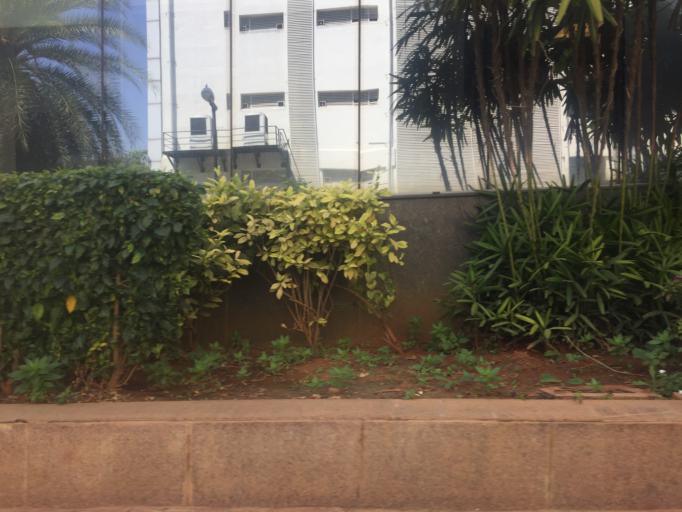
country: IN
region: Karnataka
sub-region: Bangalore Rural
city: Hoskote
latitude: 12.9815
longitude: 77.7217
